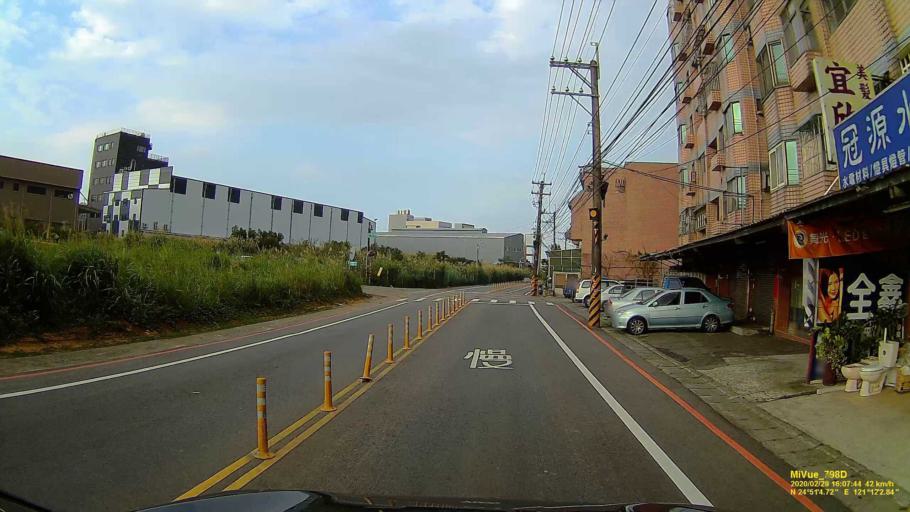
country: TW
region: Taiwan
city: Daxi
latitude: 24.8514
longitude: 121.2008
